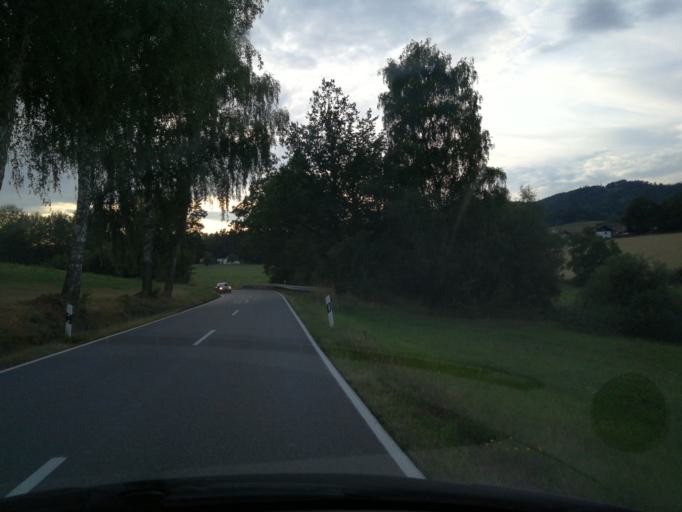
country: DE
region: Bavaria
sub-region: Lower Bavaria
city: Haibach
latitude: 49.0300
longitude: 12.7127
